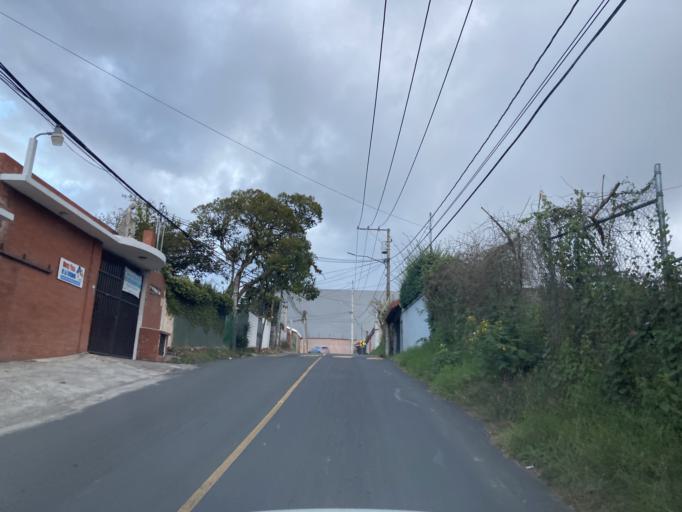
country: GT
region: Guatemala
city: Santa Catarina Pinula
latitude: 14.5571
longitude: -90.4608
